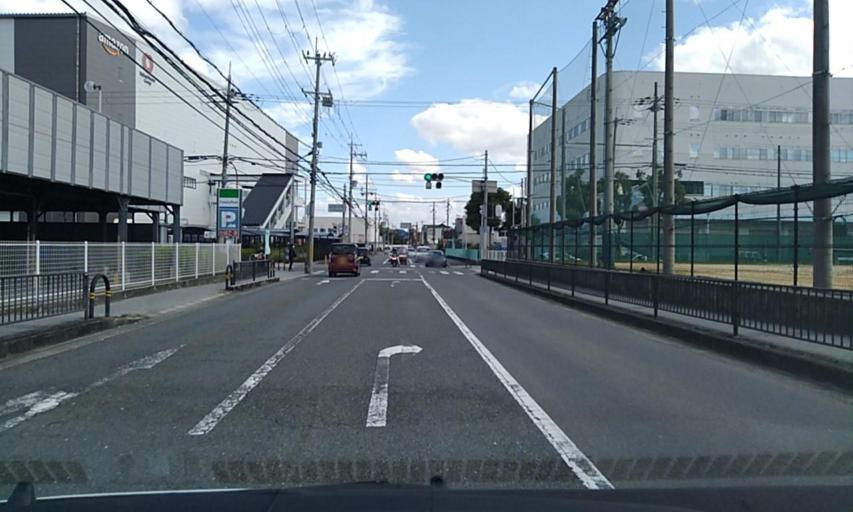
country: JP
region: Osaka
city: Ibaraki
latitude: 34.8260
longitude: 135.5653
